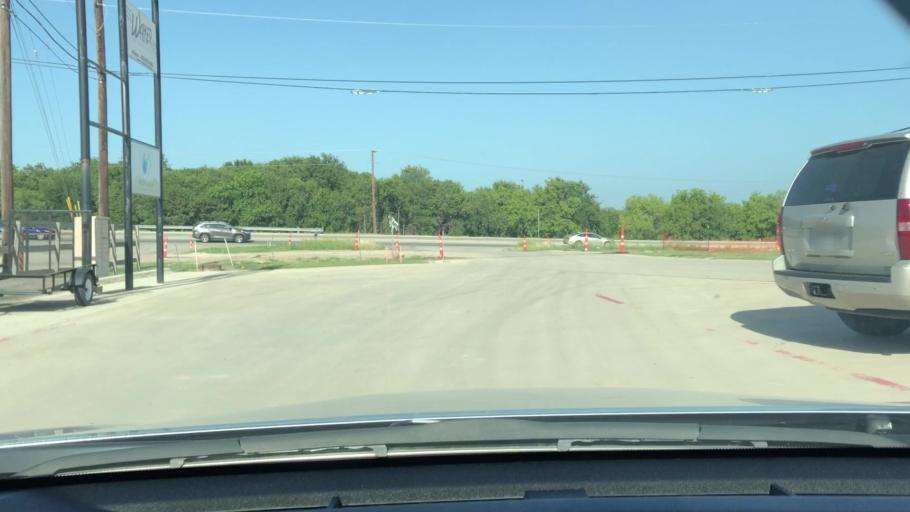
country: US
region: Texas
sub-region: Comal County
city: New Braunfels
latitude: 29.6925
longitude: -98.1561
